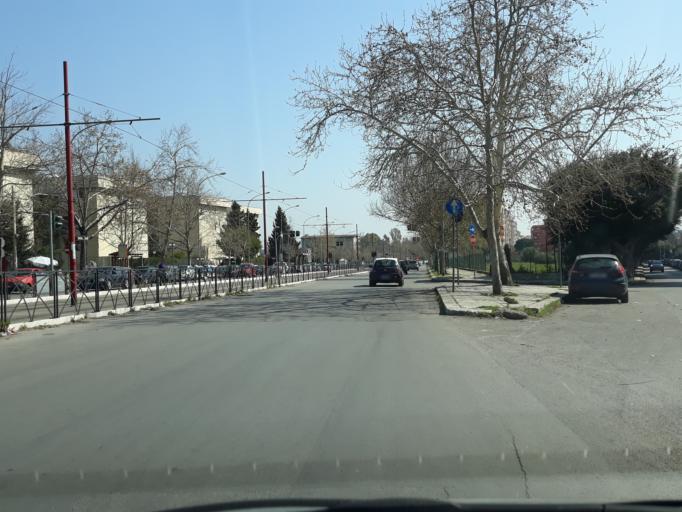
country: IT
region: Sicily
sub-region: Palermo
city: Palermo
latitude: 38.1259
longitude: 13.3036
